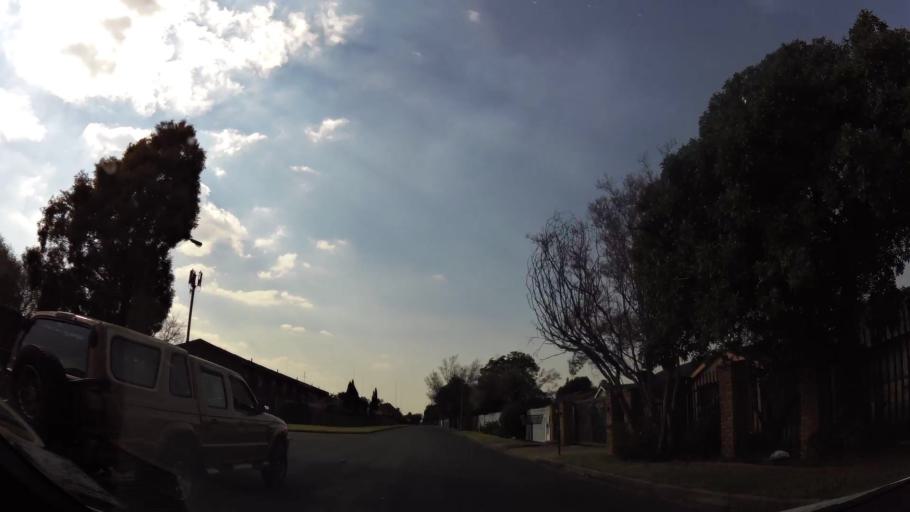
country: ZA
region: Gauteng
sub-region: Ekurhuleni Metropolitan Municipality
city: Boksburg
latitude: -26.1910
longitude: 28.2326
